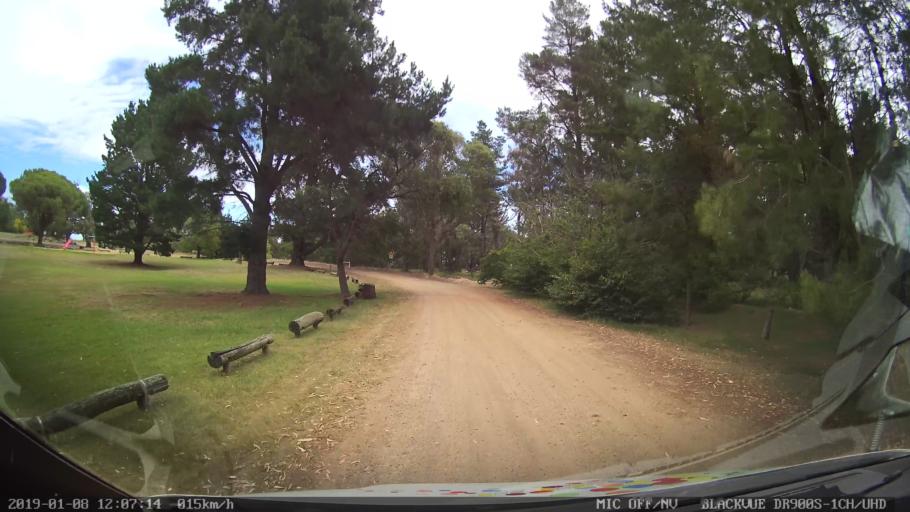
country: AU
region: New South Wales
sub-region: Armidale Dumaresq
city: Armidale
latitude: -30.4261
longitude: 151.5942
